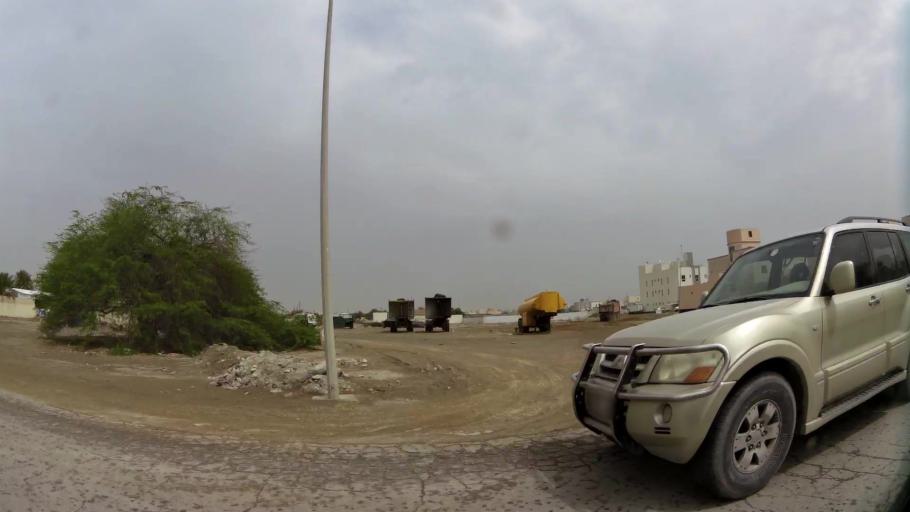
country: BH
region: Northern
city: Ar Rifa'
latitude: 26.1315
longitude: 50.5912
